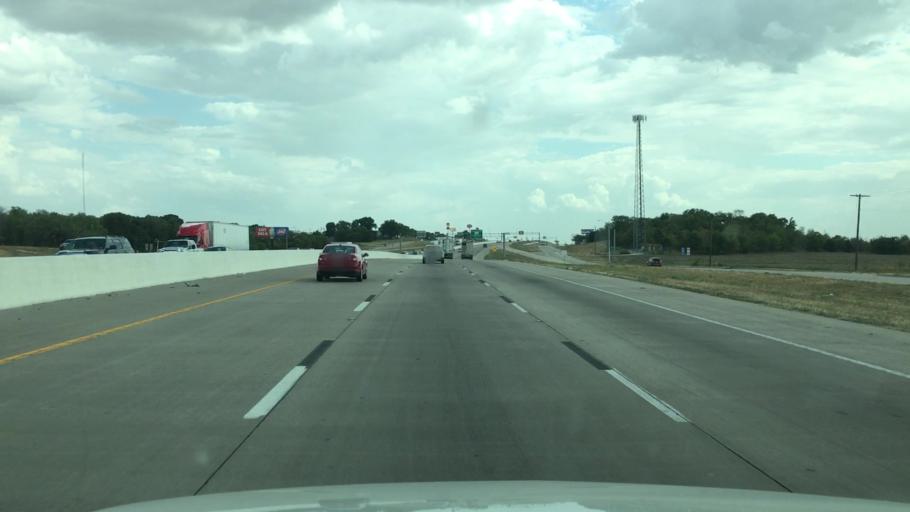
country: US
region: Texas
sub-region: McLennan County
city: West
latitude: 31.8126
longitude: -97.0986
